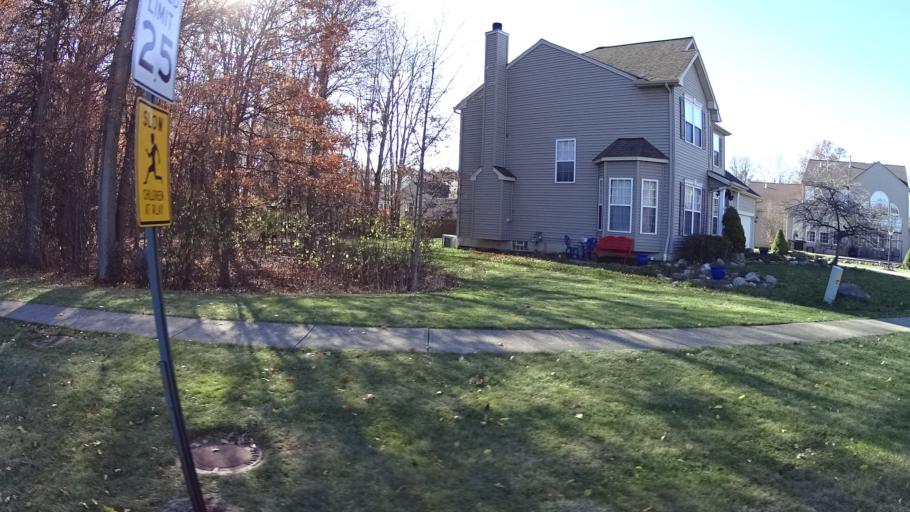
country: US
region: Ohio
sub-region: Lorain County
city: Avon Center
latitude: 41.4644
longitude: -81.9801
